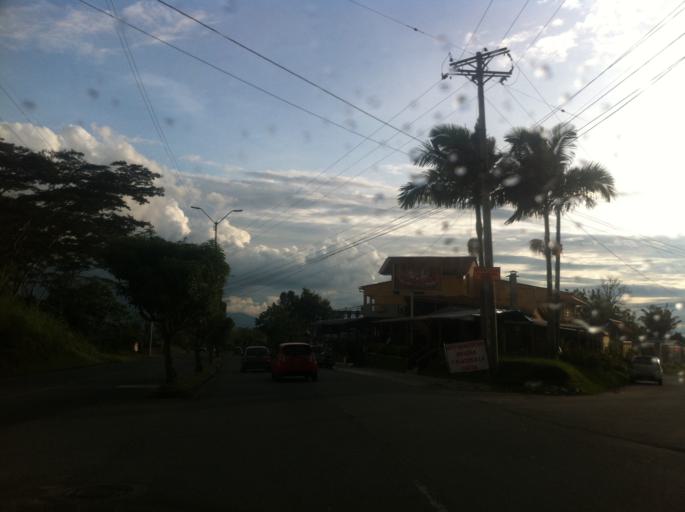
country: CO
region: Quindio
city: Calarca
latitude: 4.5683
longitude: -75.6419
